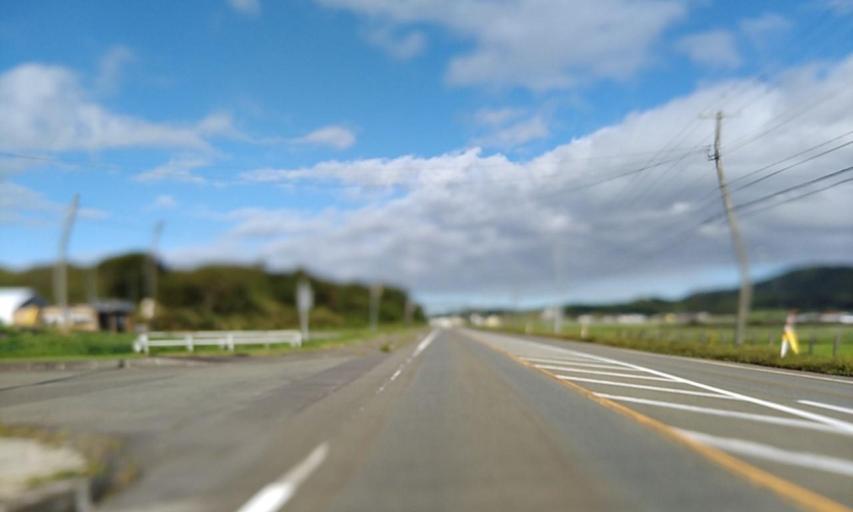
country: JP
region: Hokkaido
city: Shizunai-furukawacho
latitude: 42.2217
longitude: 142.6338
